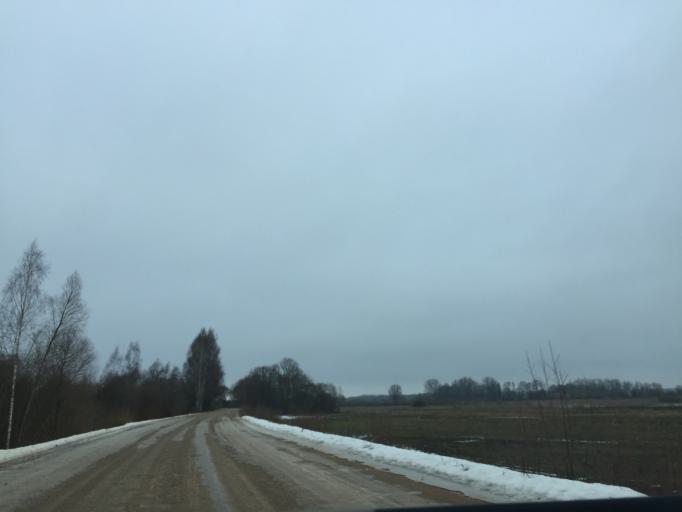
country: LV
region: Ozolnieku
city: Ozolnieki
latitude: 56.6329
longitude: 23.8041
